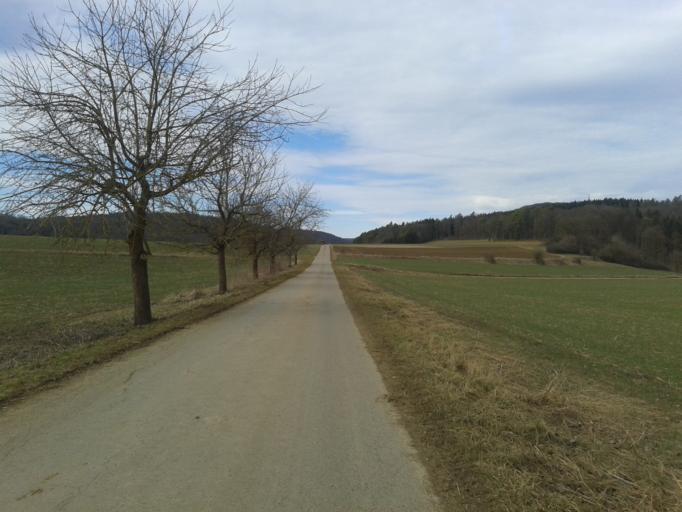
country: DE
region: Baden-Wuerttemberg
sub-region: Tuebingen Region
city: Schelklingen
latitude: 48.3519
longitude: 9.7471
